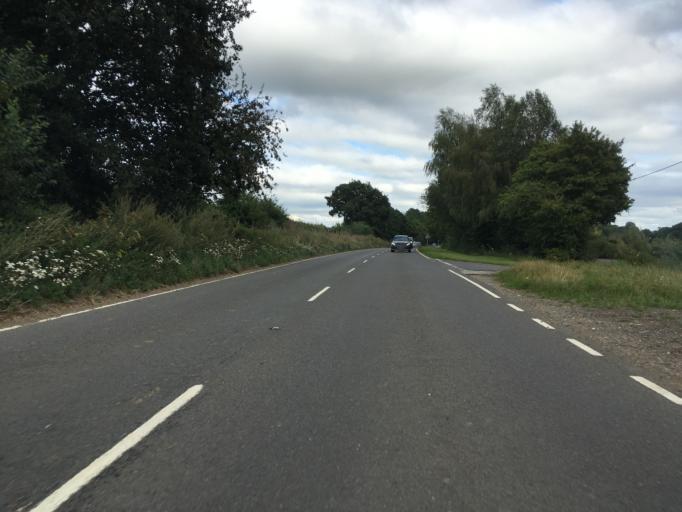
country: GB
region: England
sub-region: Hampshire
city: Liss
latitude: 51.0066
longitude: -0.8693
